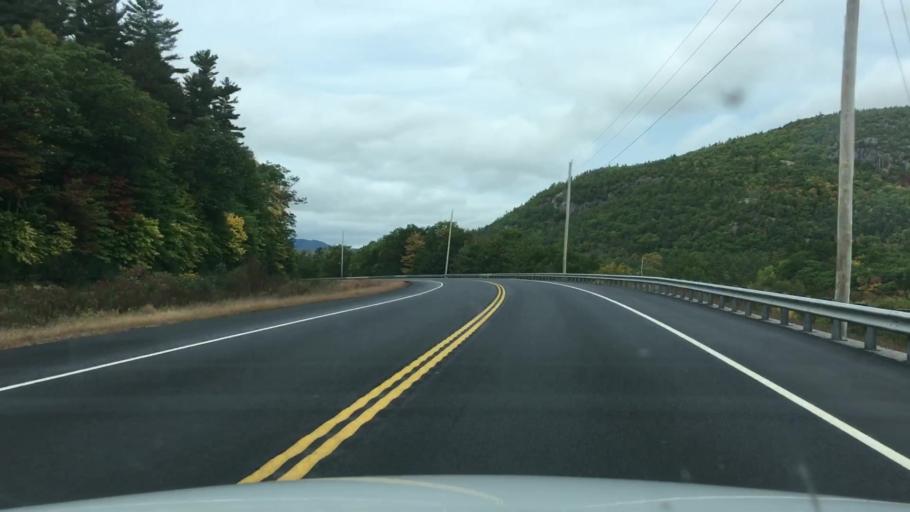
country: US
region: Maine
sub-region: Oxford County
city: Bethel
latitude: 44.4052
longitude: -70.9217
